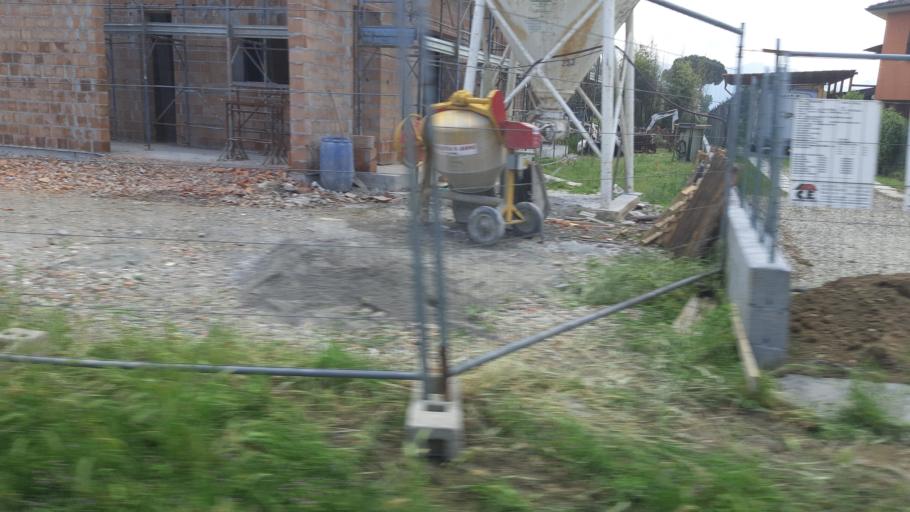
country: IT
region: Tuscany
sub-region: Provincia di Lucca
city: Capannori
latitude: 43.8637
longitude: 10.5541
